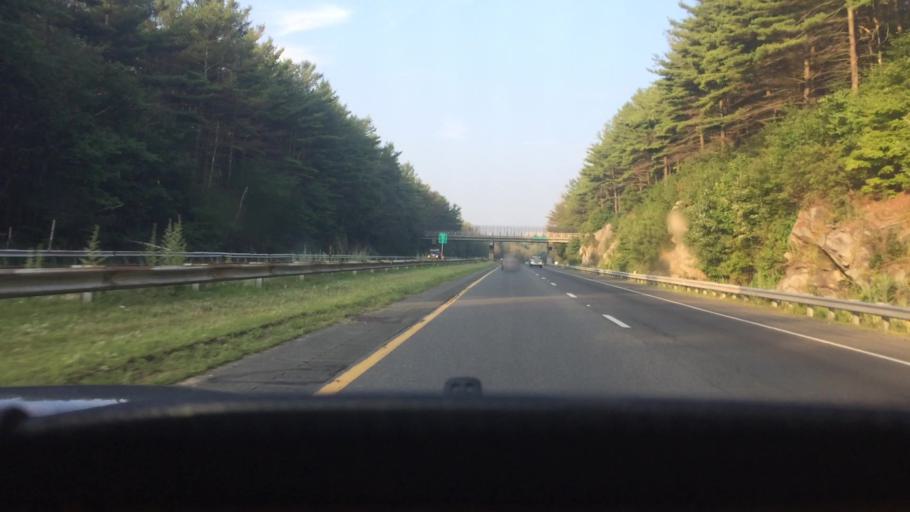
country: US
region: Massachusetts
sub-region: Hampden County
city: Three Rivers
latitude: 42.1612
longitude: -72.3619
